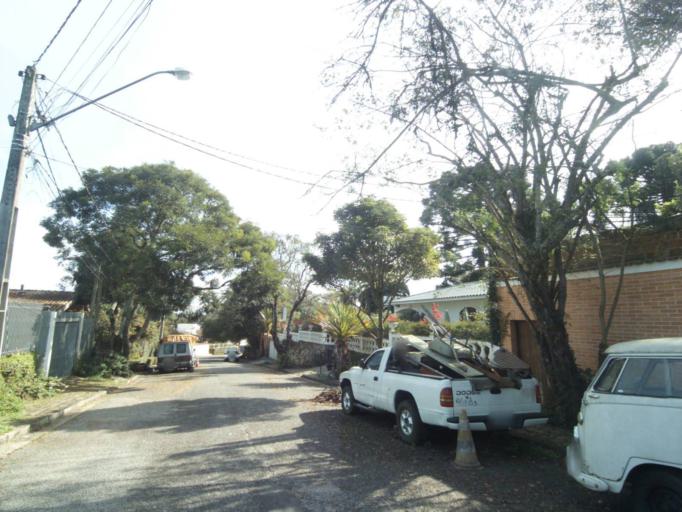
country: BR
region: Parana
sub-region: Curitiba
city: Curitiba
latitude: -25.4162
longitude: -49.2996
